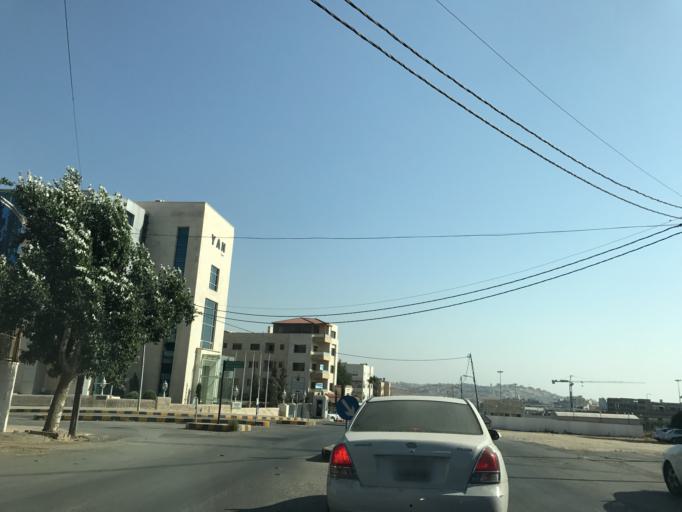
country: JO
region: Amman
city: Wadi as Sir
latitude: 31.9481
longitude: 35.8518
